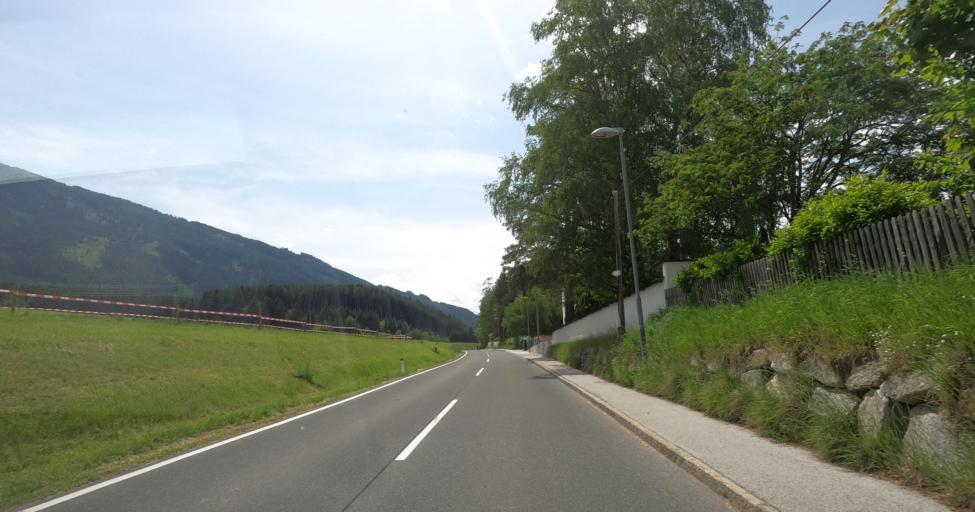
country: AT
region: Tyrol
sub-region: Politischer Bezirk Innsbruck Land
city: Sistrans
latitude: 47.2341
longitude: 11.4320
